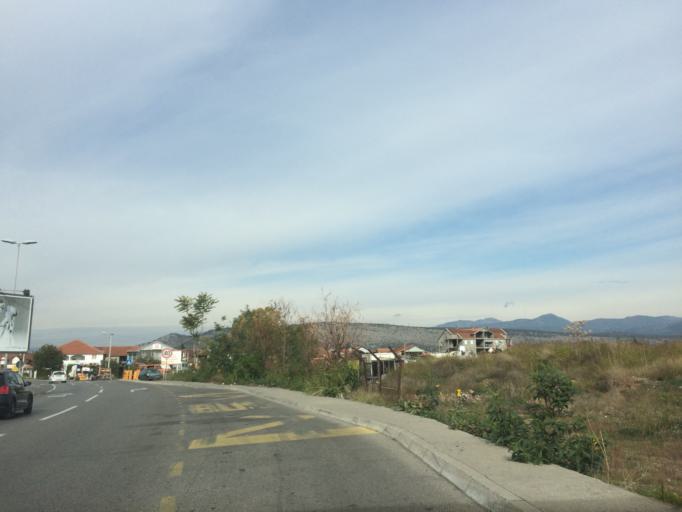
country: ME
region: Podgorica
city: Podgorica
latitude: 42.4371
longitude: 19.2270
